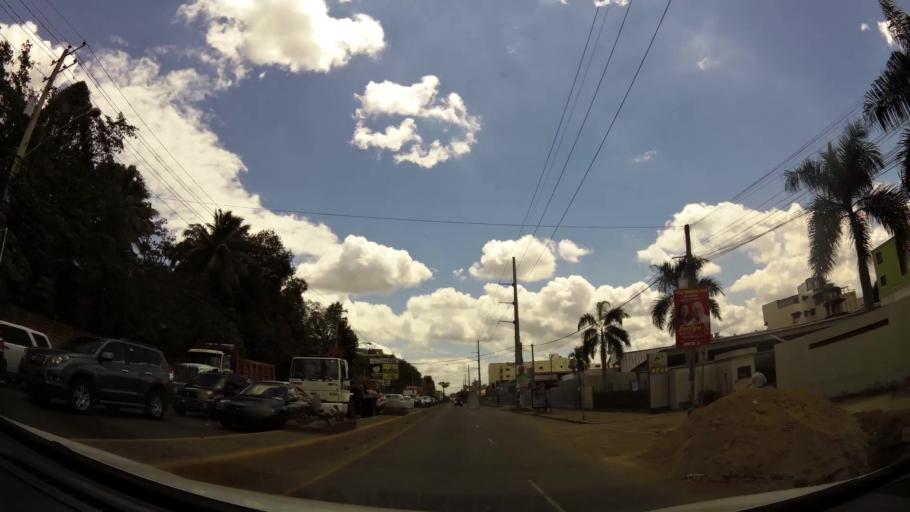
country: DO
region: Santiago
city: Santiago de los Caballeros
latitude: 19.4678
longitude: -70.6871
